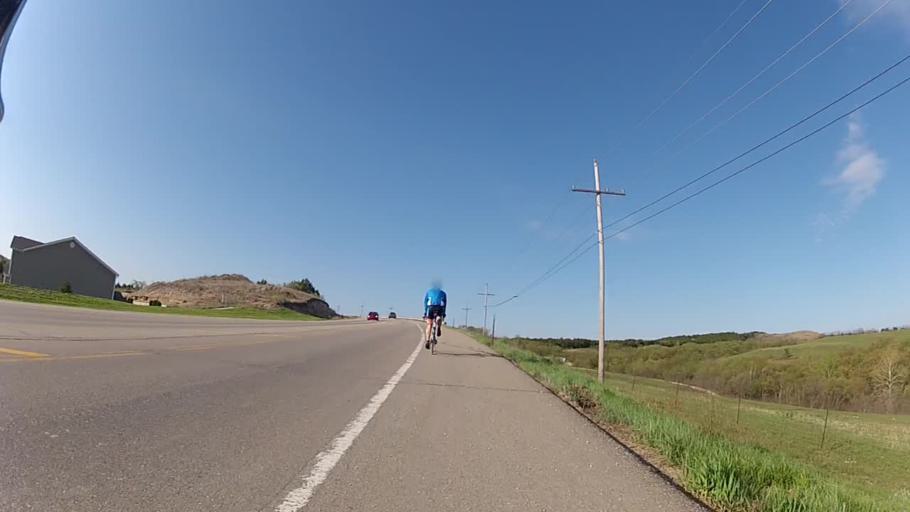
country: US
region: Kansas
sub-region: Riley County
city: Manhattan
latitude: 39.1781
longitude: -96.6474
